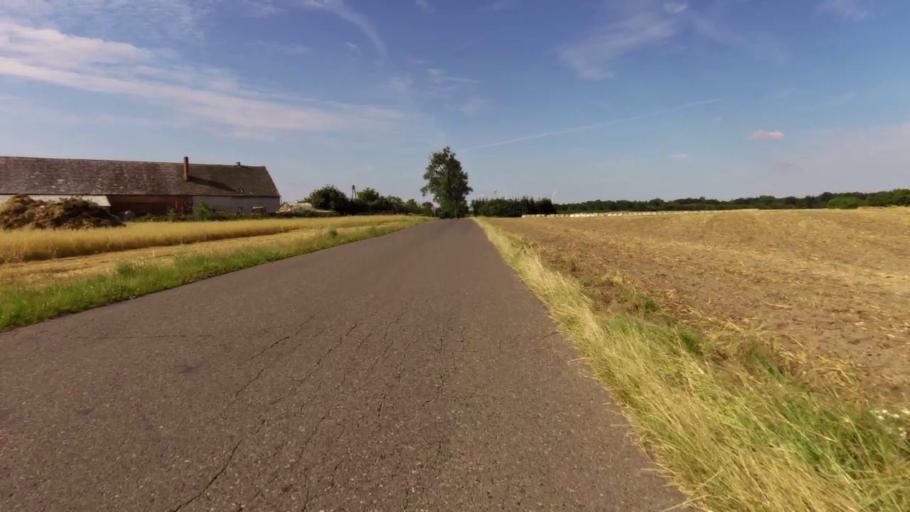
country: PL
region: West Pomeranian Voivodeship
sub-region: Powiat stargardzki
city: Marianowo
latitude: 53.3492
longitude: 15.1980
